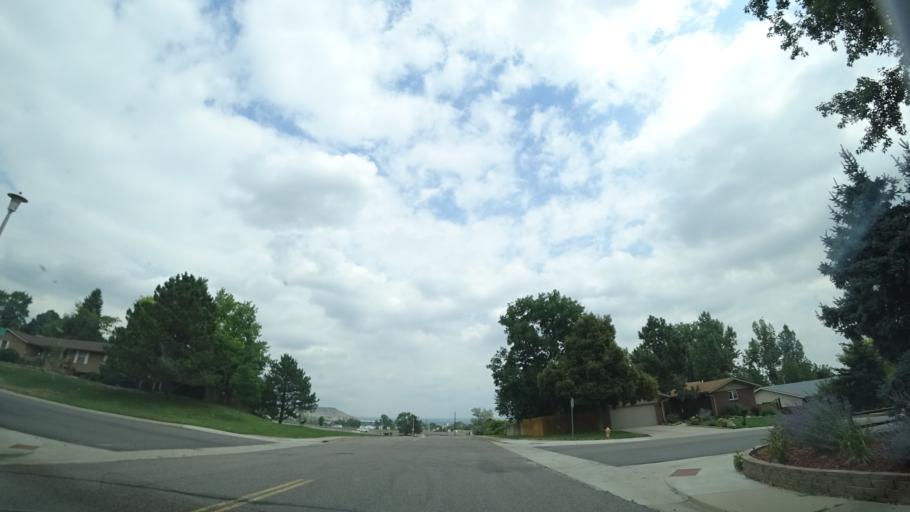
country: US
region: Colorado
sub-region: Jefferson County
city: West Pleasant View
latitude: 39.7232
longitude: -105.1596
